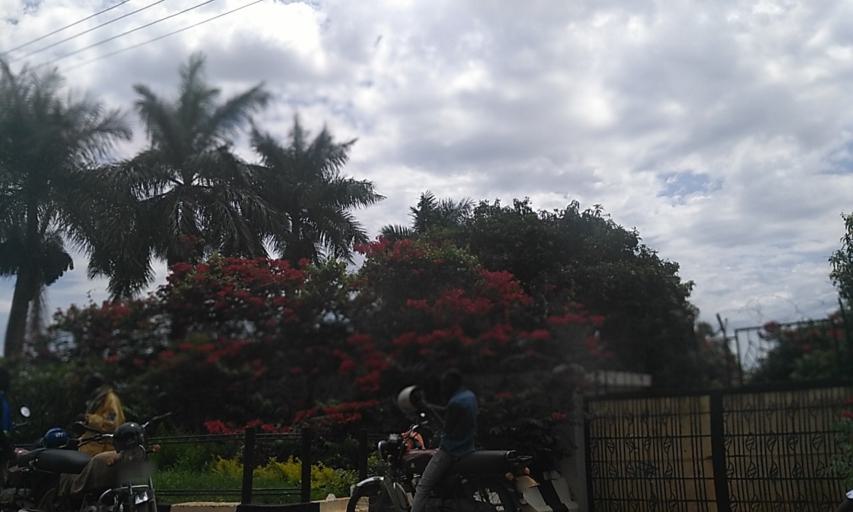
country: UG
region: Central Region
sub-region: Kampala District
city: Kampala
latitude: 0.3275
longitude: 32.5908
